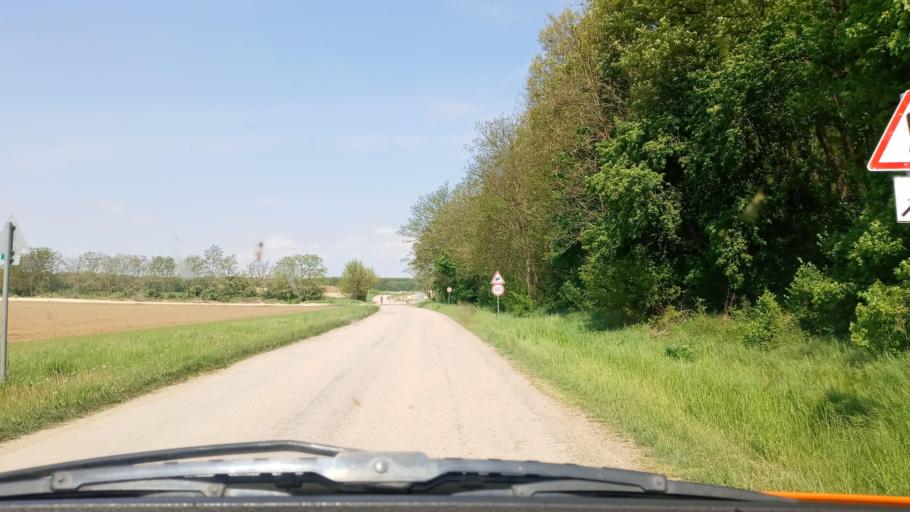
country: HU
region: Baranya
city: Boly
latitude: 45.8852
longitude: 18.5676
